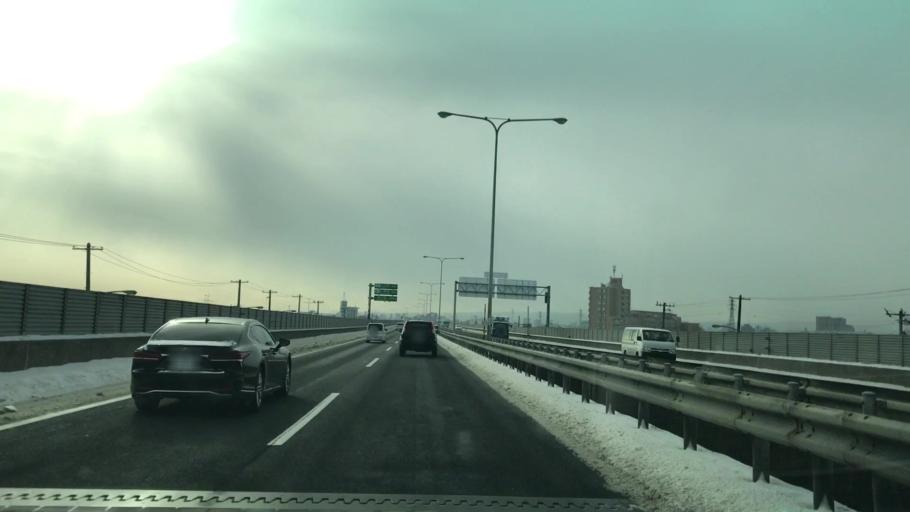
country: JP
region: Hokkaido
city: Sapporo
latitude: 43.0665
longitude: 141.4232
